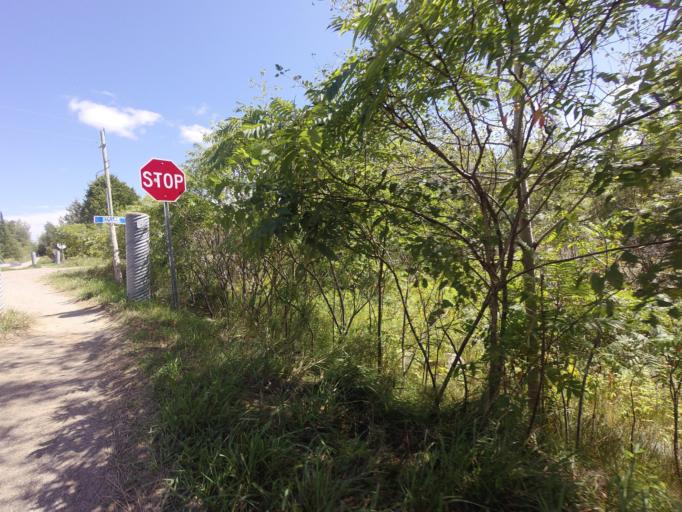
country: CA
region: Ontario
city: Orangeville
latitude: 43.7772
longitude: -80.1749
